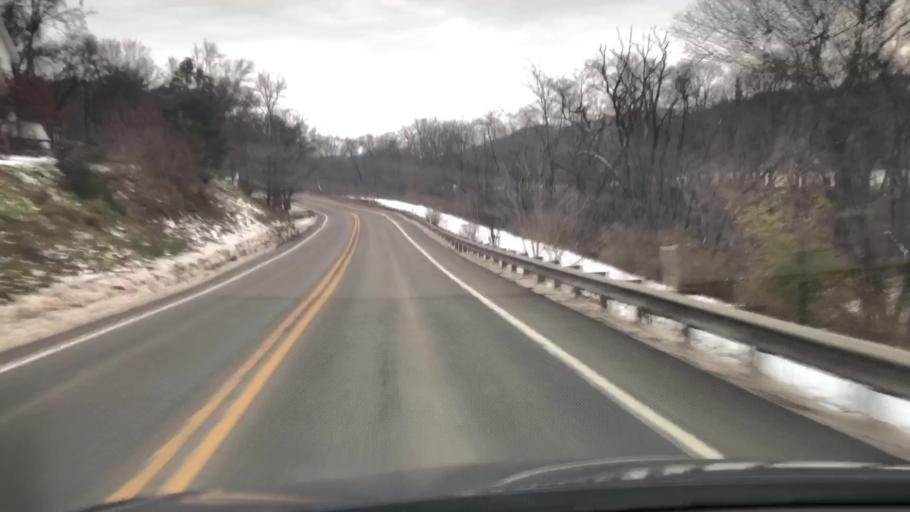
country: US
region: Pennsylvania
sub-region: Clarion County
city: Clarion
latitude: 41.0226
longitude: -79.2683
